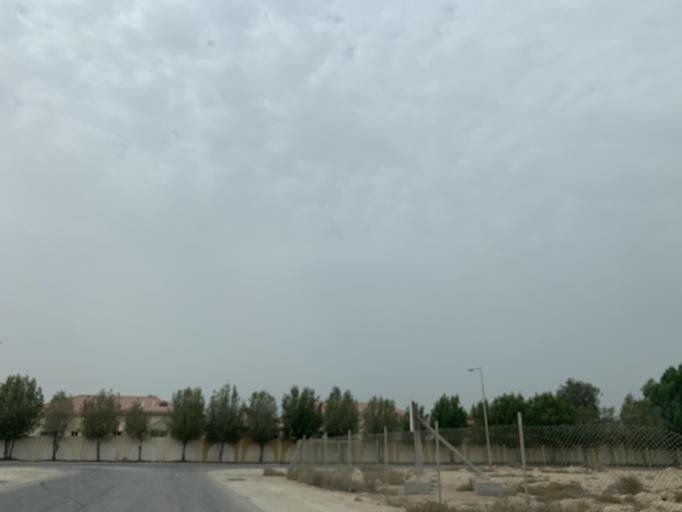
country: BH
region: Central Governorate
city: Madinat Hamad
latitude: 26.1796
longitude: 50.4712
